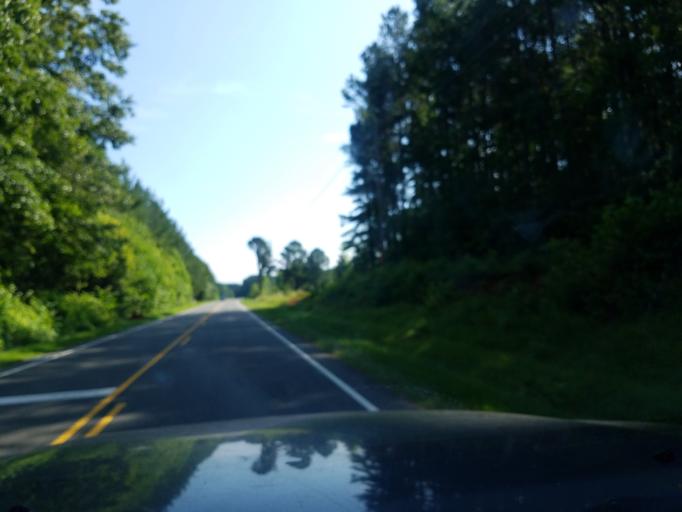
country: US
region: North Carolina
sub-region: Granville County
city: Oxford
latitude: 36.2730
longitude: -78.6448
